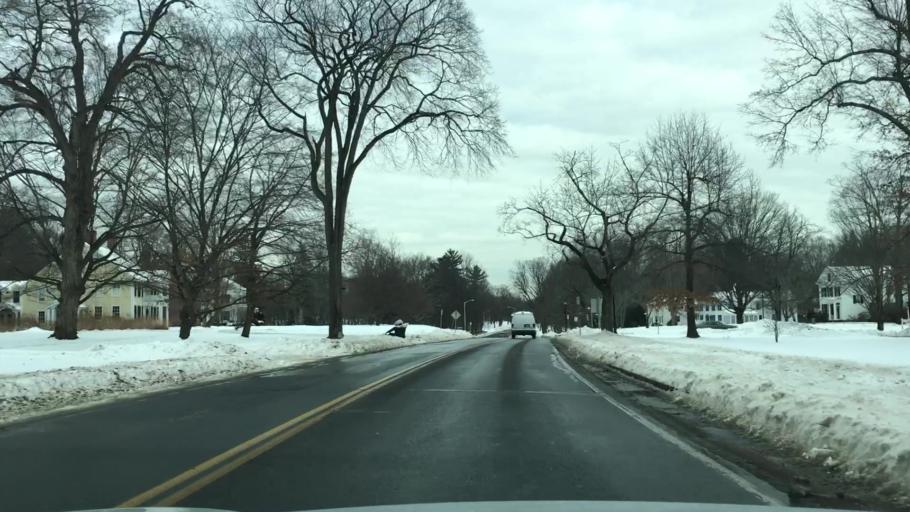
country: US
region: Massachusetts
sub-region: Hampden County
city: Longmeadow
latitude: 42.0513
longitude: -72.5827
